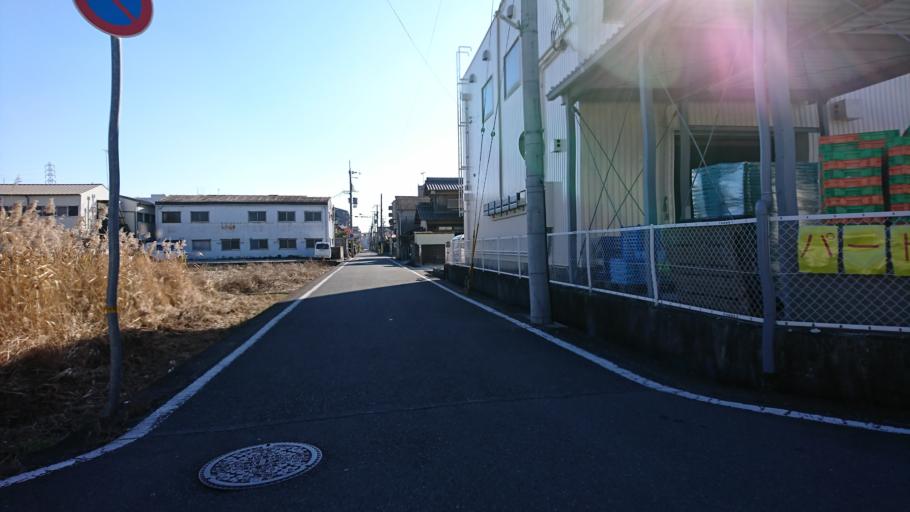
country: JP
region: Hyogo
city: Kakogawacho-honmachi
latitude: 34.7325
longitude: 134.8456
